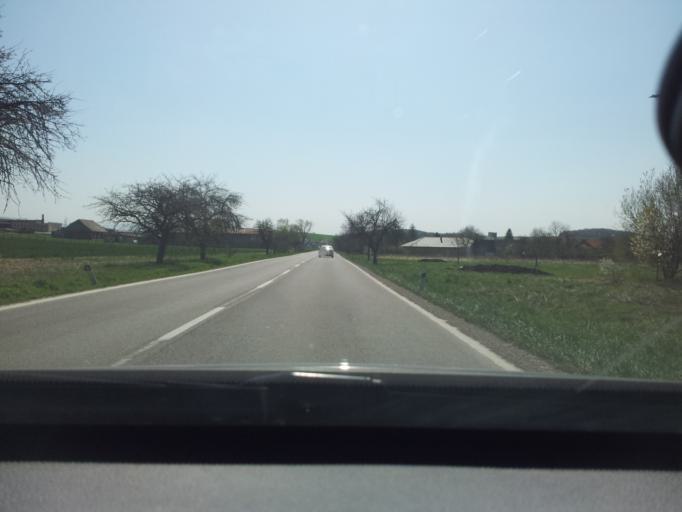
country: SK
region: Nitriansky
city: Banovce nad Bebravou
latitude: 48.7864
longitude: 18.1696
